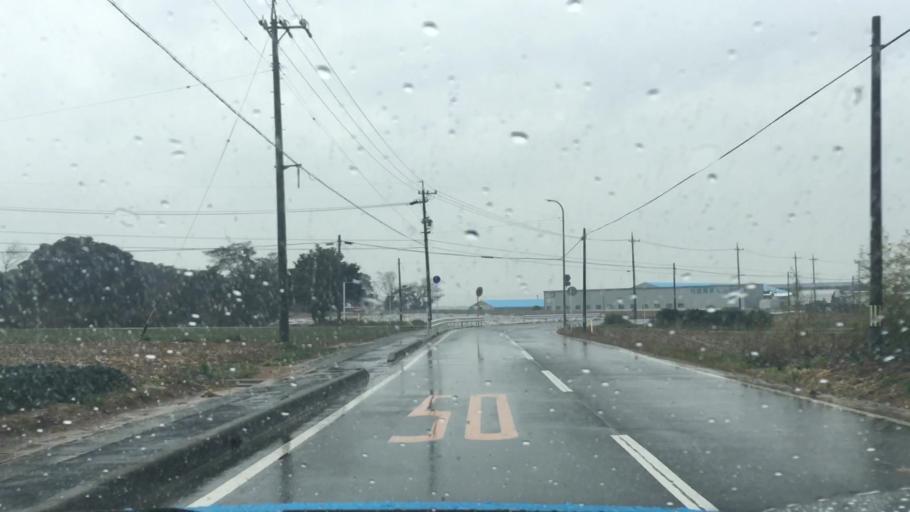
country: JP
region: Aichi
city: Tahara
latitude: 34.6475
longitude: 137.2974
